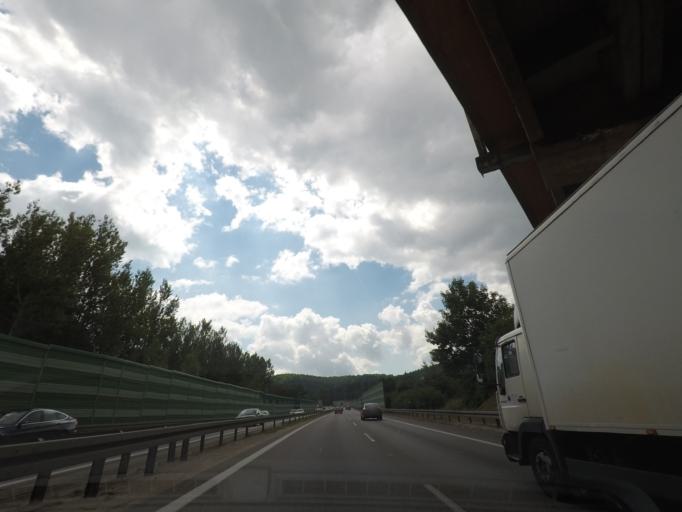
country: PL
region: Pomeranian Voivodeship
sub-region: Gdynia
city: Pogorze
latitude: 54.5348
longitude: 18.4550
